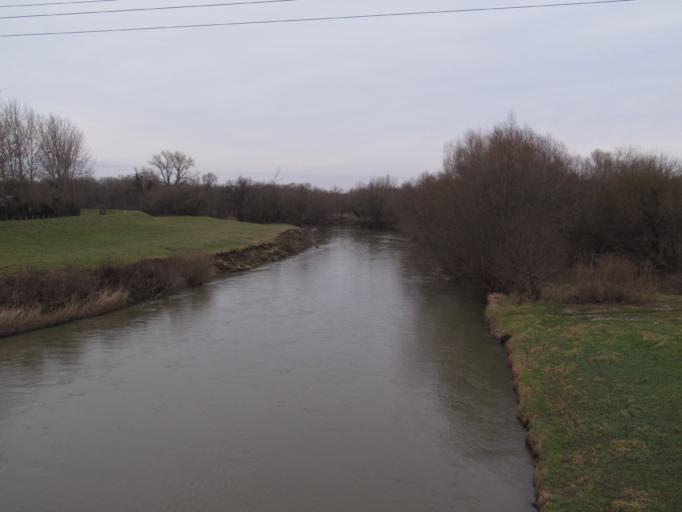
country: HU
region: Vas
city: Sarvar
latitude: 47.2463
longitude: 16.9539
